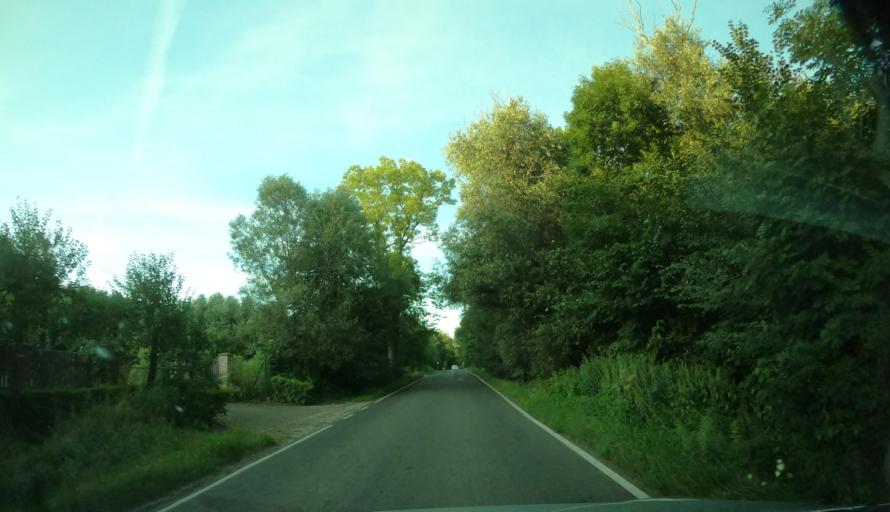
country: PL
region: Kujawsko-Pomorskie
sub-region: Bydgoszcz
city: Fordon
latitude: 53.2242
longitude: 18.1919
